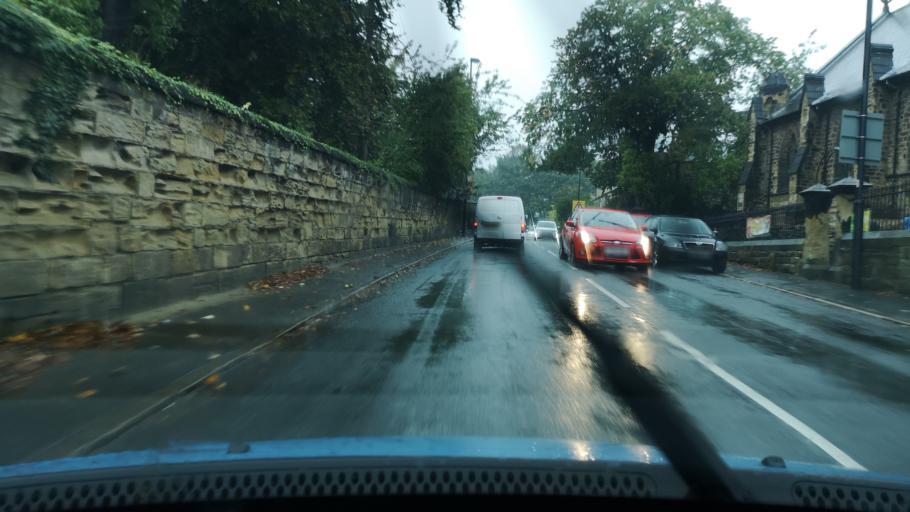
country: GB
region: England
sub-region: City and Borough of Wakefield
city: Low Ackworth
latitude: 53.6484
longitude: -1.3327
